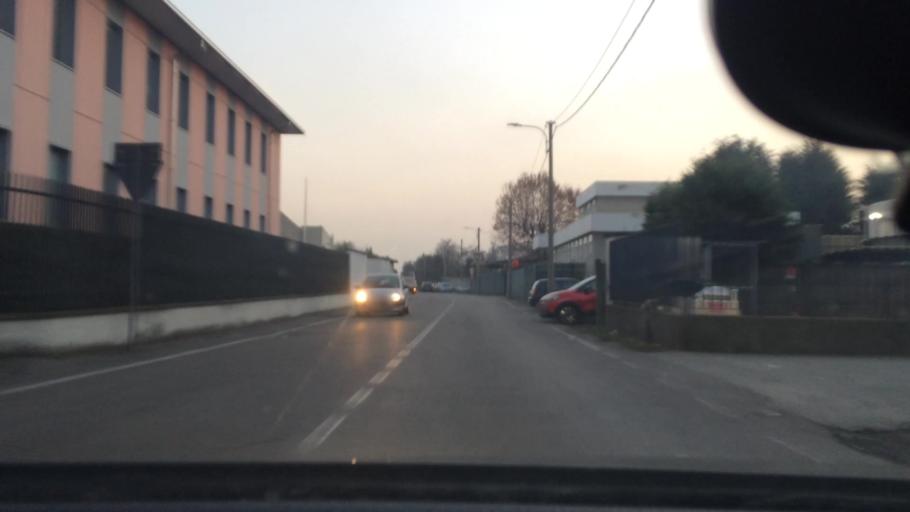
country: IT
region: Lombardy
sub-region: Provincia di Varese
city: Caronno Pertusella
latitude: 45.6078
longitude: 9.0437
